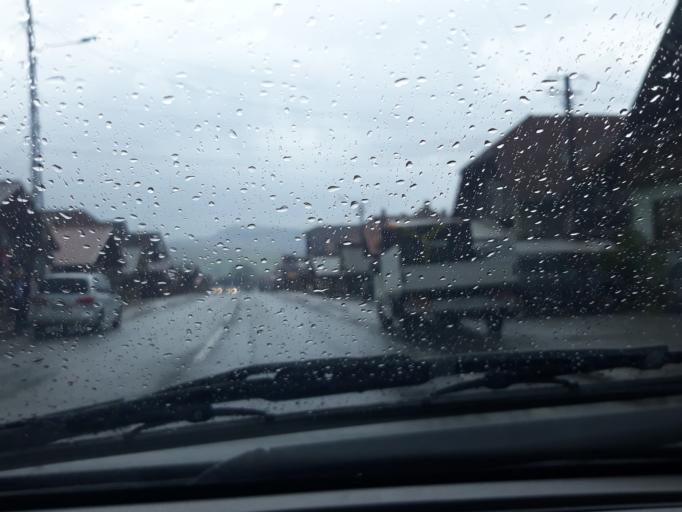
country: RO
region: Harghita
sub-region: Comuna Corund
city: Corund
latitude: 46.4730
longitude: 25.1821
